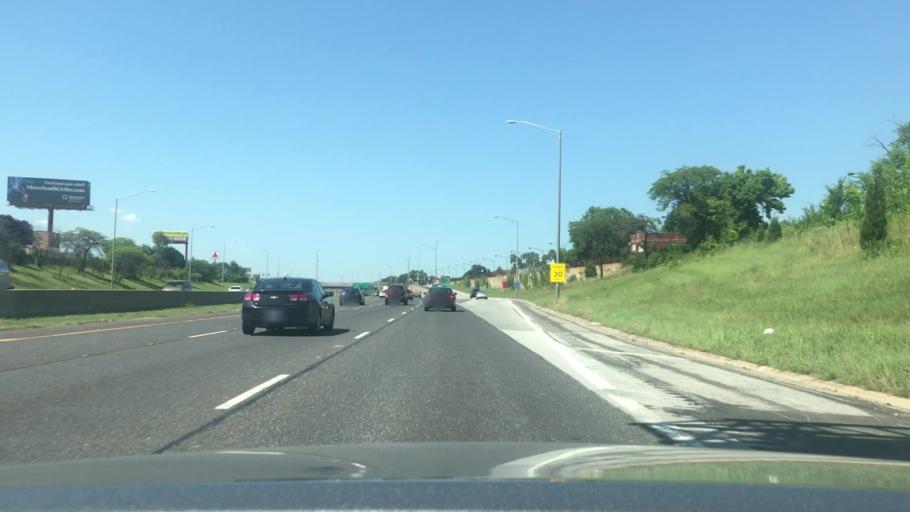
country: US
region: Illinois
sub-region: Cook County
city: Calumet Park
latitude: 41.6725
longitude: -87.6618
